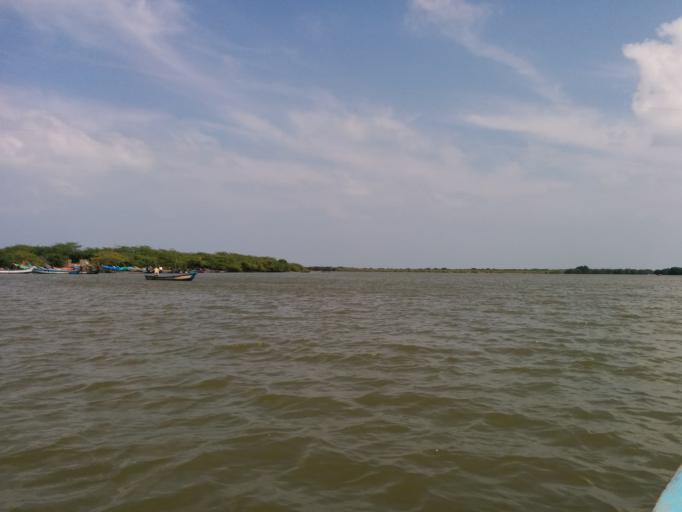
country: IN
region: Tamil Nadu
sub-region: Cuddalore
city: Annamalainagar
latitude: 11.4310
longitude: 79.7822
